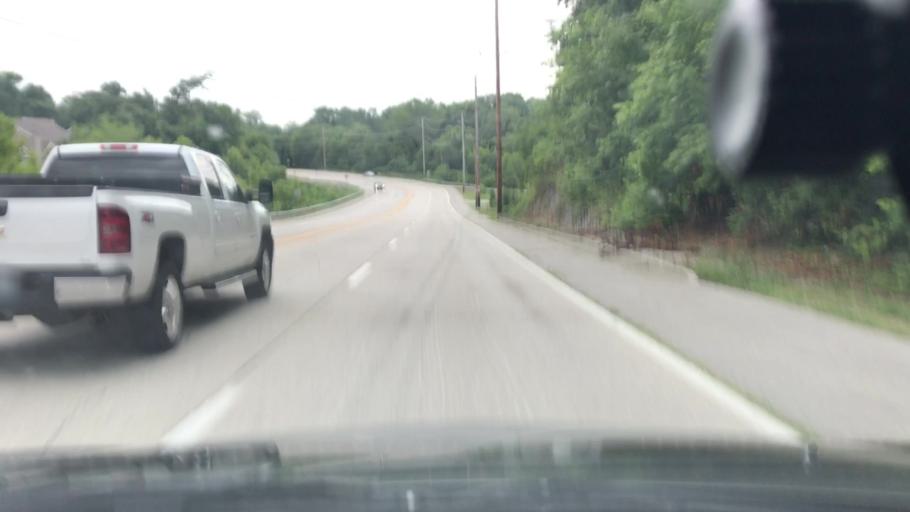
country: US
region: Missouri
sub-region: Saint Charles County
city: Saint Charles
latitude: 38.7429
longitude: -90.5205
